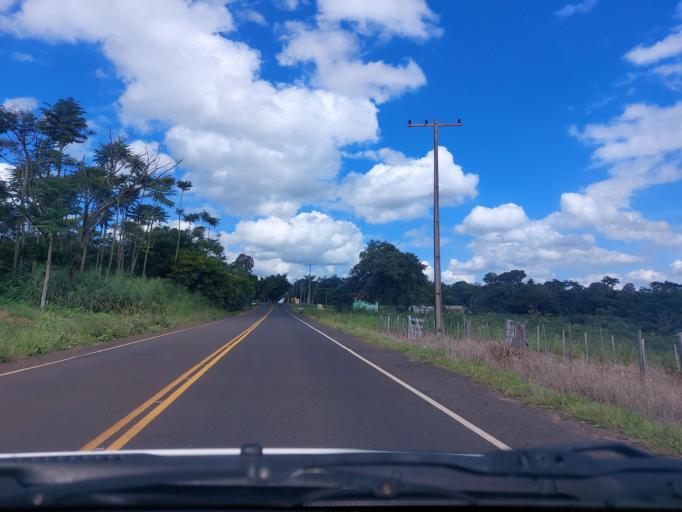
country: PY
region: San Pedro
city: Guayaybi
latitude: -24.5648
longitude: -56.5195
